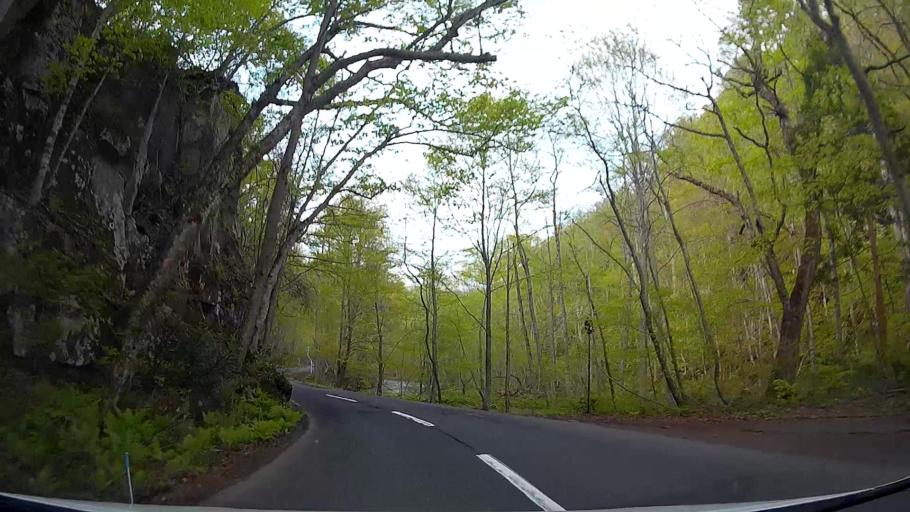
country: JP
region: Aomori
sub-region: Aomori Shi
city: Furudate
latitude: 40.5261
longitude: 140.9743
